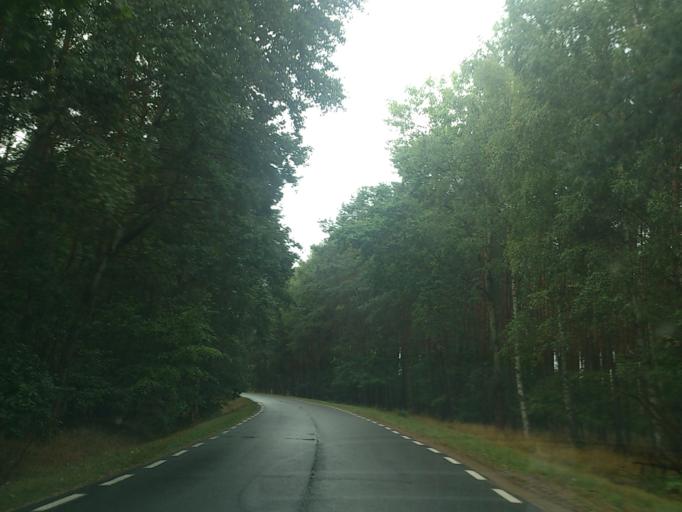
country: PL
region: Greater Poland Voivodeship
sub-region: Powiat poznanski
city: Pobiedziska
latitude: 52.5141
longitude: 17.1987
